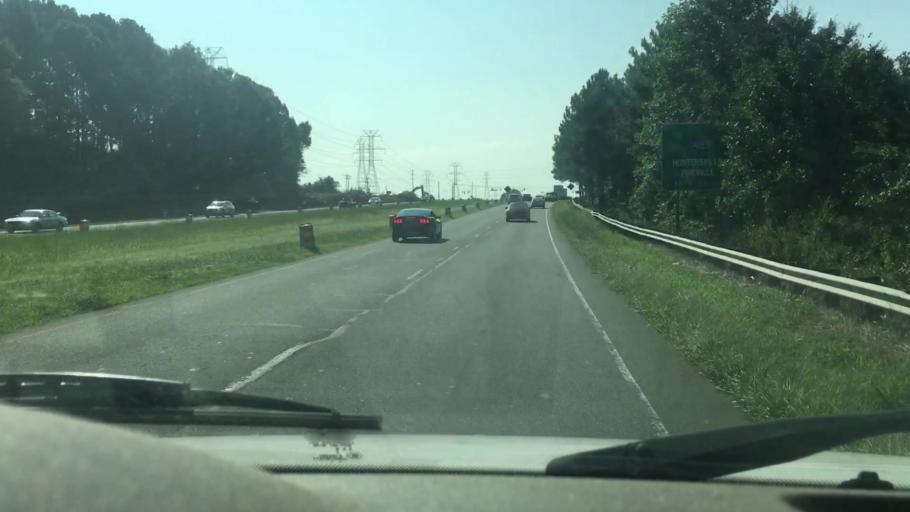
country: US
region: North Carolina
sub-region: Gaston County
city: Mount Holly
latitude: 35.3281
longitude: -80.9487
